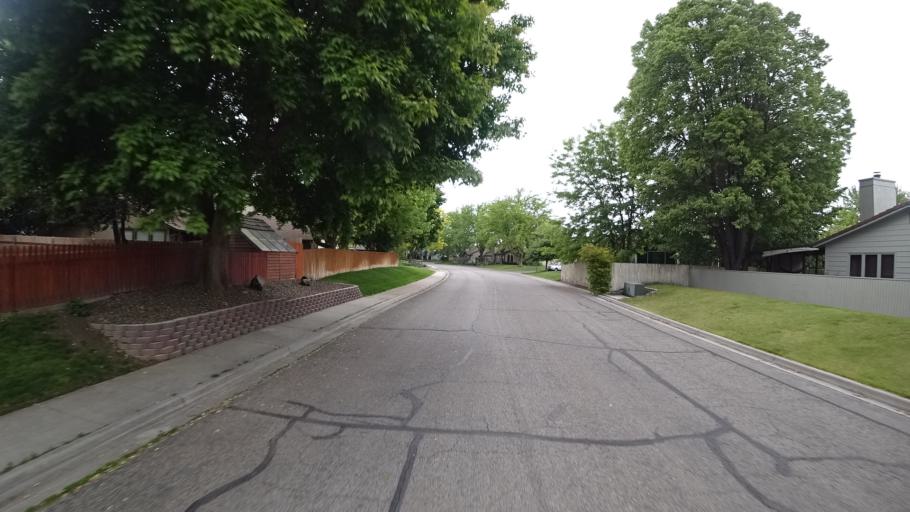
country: US
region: Idaho
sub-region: Ada County
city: Garden City
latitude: 43.6689
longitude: -116.2597
